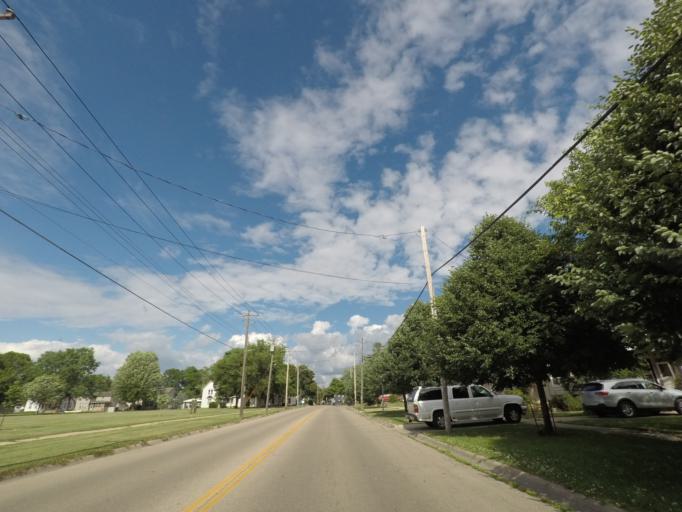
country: US
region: Wisconsin
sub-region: Rock County
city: Janesville
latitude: 42.6743
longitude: -89.0241
